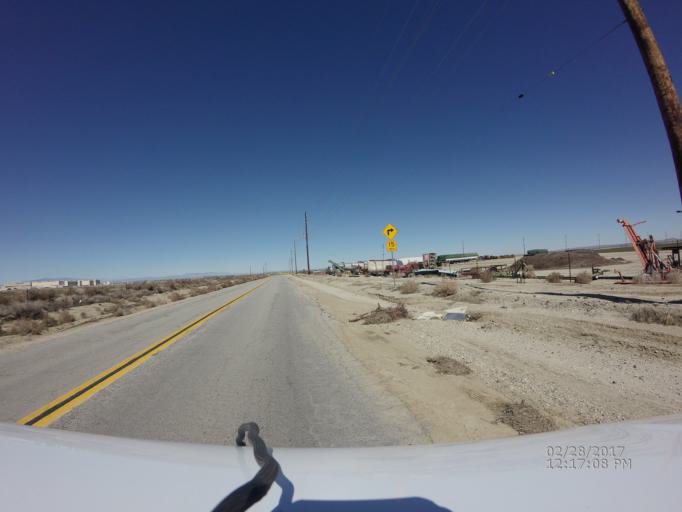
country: US
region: California
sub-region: Los Angeles County
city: Palmdale
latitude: 34.6294
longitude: -118.0587
